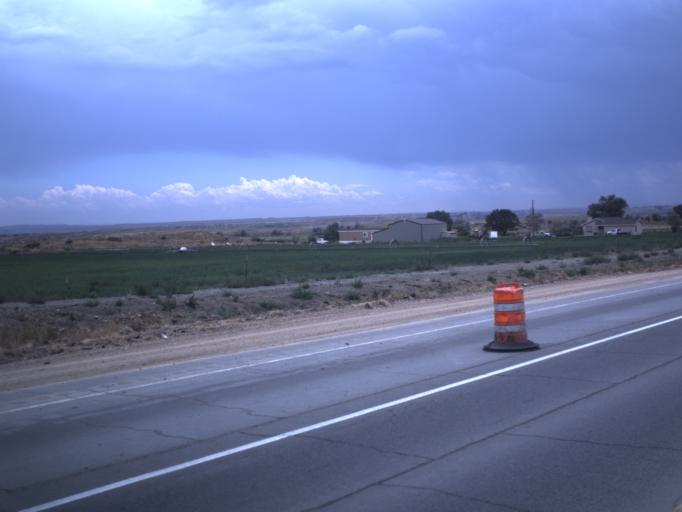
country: US
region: Utah
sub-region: Duchesne County
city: Roosevelt
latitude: 40.2247
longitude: -110.0674
